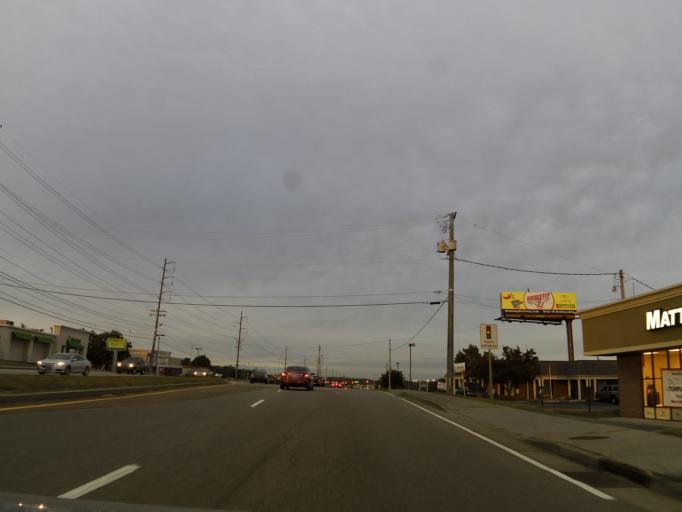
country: US
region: Tennessee
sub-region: Blount County
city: Louisville
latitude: 35.9259
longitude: -84.0444
